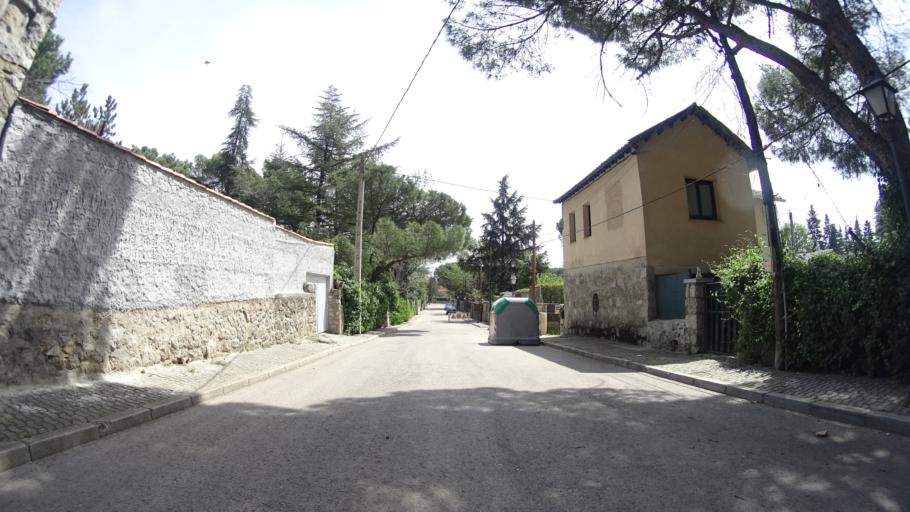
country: ES
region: Madrid
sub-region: Provincia de Madrid
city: Torrelodones
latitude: 40.5811
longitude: -3.9542
